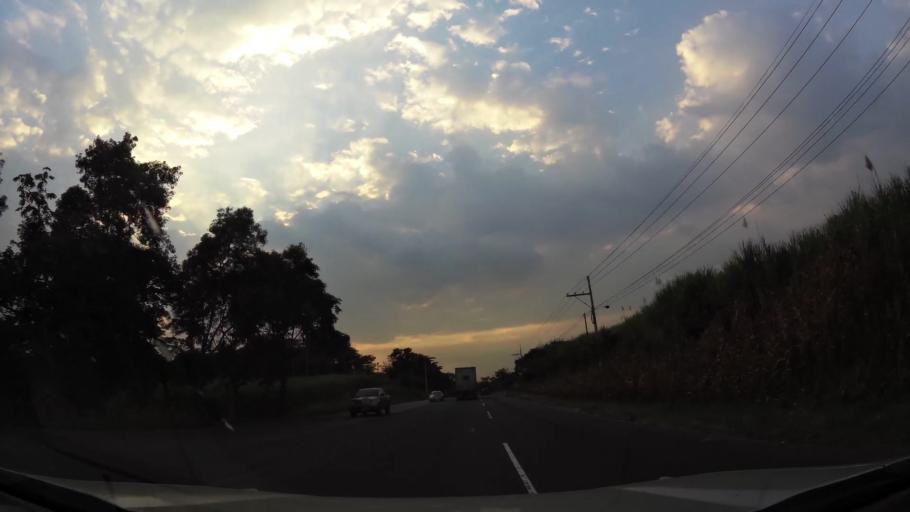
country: GT
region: Escuintla
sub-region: Municipio de La Democracia
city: La Democracia
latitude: 14.2671
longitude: -90.8848
